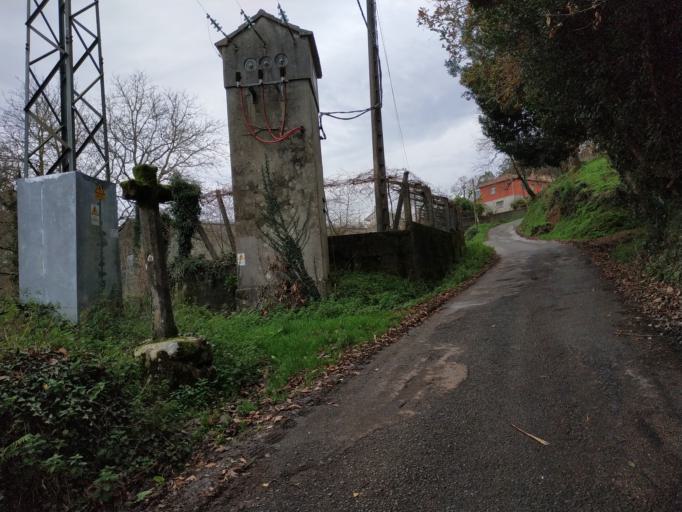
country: ES
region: Galicia
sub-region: Provincia de Pontevedra
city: Silleda
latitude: 42.7790
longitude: -8.1700
